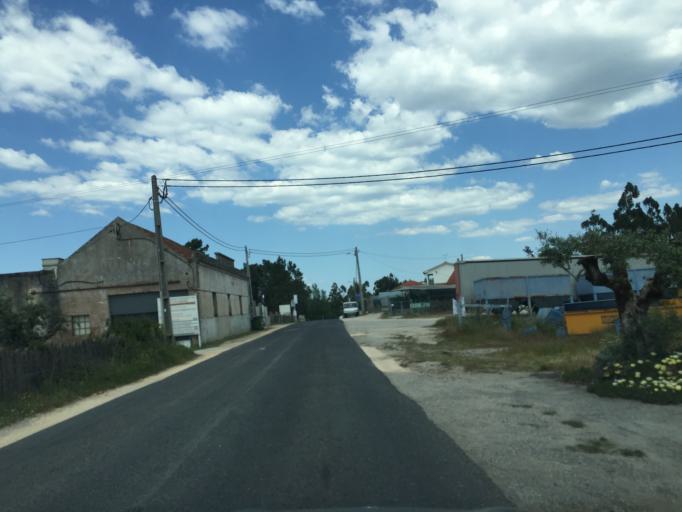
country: PT
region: Santarem
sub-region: Ourem
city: Ourem
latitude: 39.6908
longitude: -8.5439
